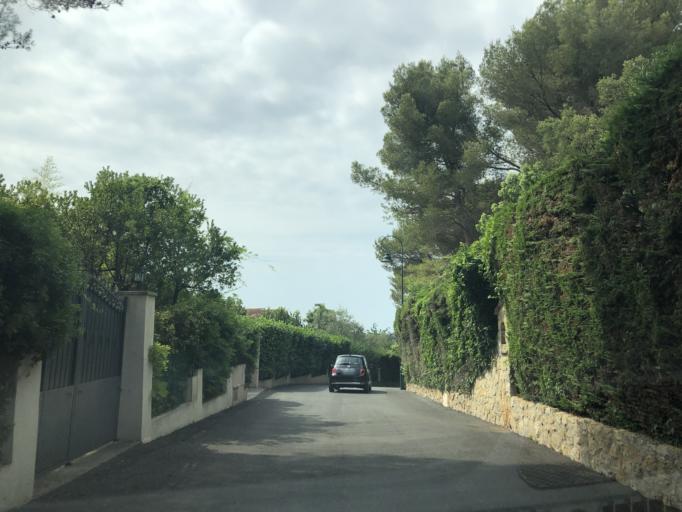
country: FR
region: Provence-Alpes-Cote d'Azur
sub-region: Departement des Alpes-Maritimes
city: Biot
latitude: 43.6207
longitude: 7.0831
